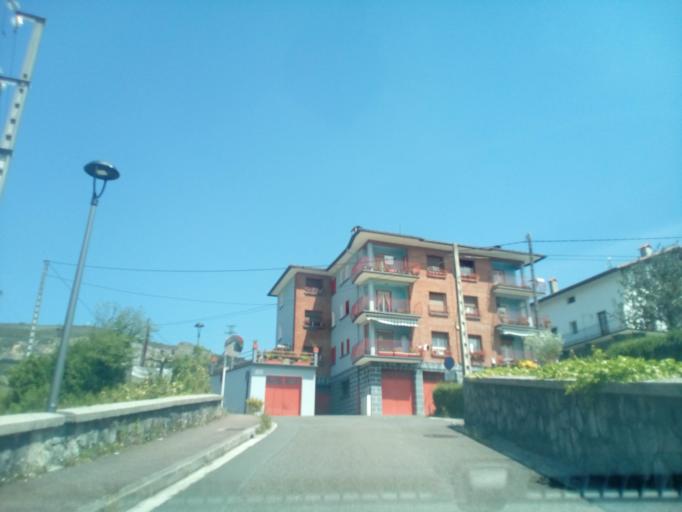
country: ES
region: Basque Country
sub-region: Provincia de Guipuzcoa
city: Andoain
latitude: 43.2227
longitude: -2.0183
